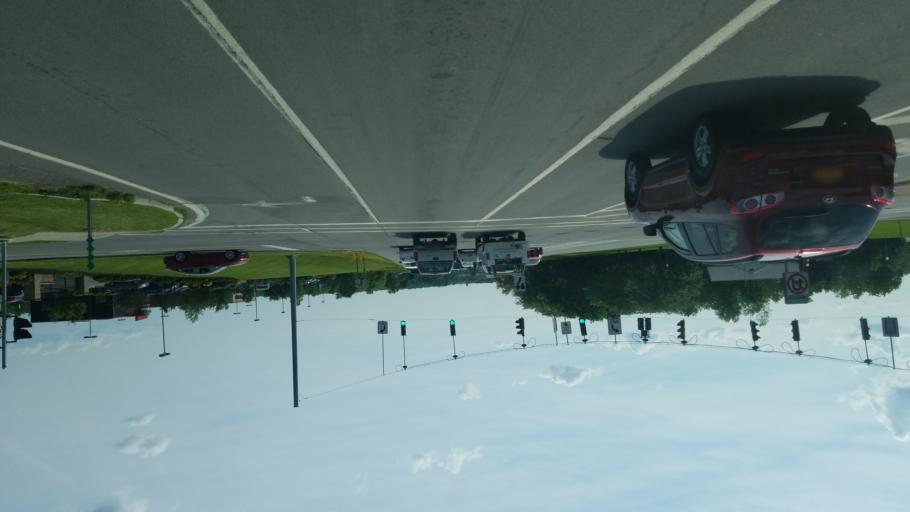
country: US
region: New York
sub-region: Ontario County
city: Canandaigua
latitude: 42.8722
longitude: -77.2397
